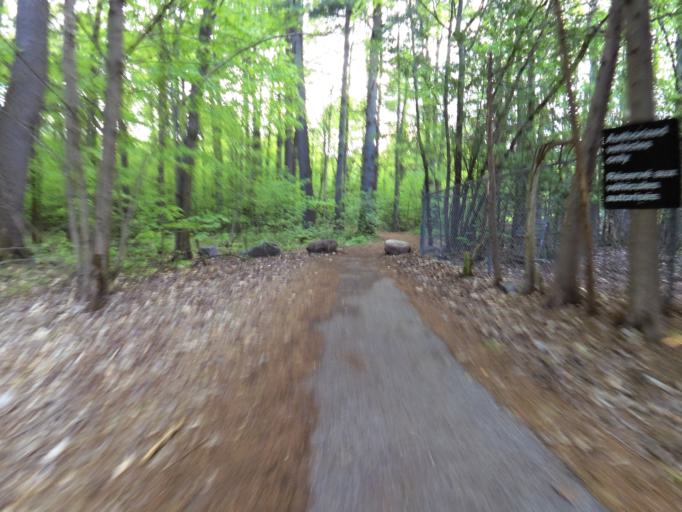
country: CA
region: Ontario
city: Bells Corners
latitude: 45.3245
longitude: -75.8120
